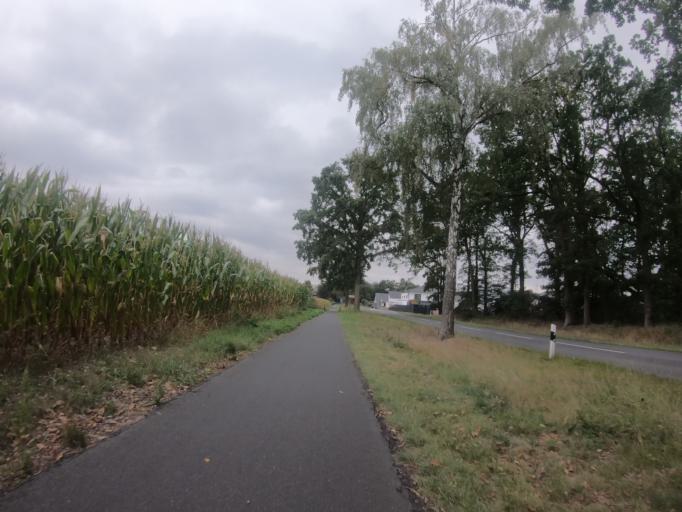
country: DE
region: Lower Saxony
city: Ribbesbuttel
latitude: 52.4369
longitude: 10.5054
